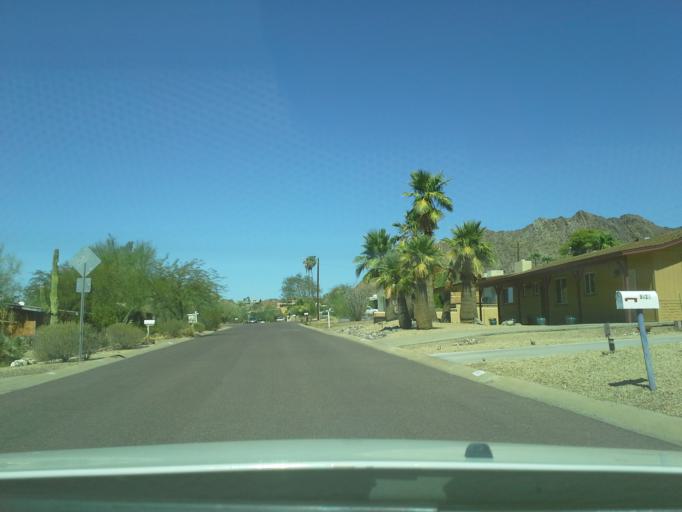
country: US
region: Arizona
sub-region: Maricopa County
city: Paradise Valley
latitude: 33.5721
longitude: -112.0471
